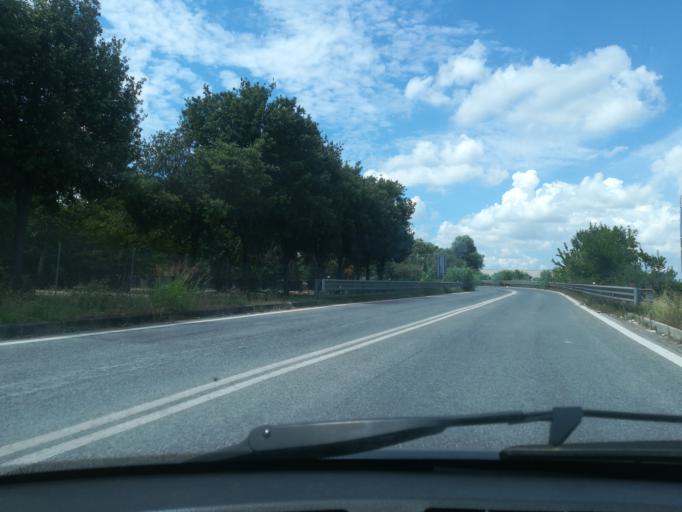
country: IT
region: The Marches
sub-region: Provincia di Macerata
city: Santa Maria Apparente
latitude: 43.2809
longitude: 13.6846
